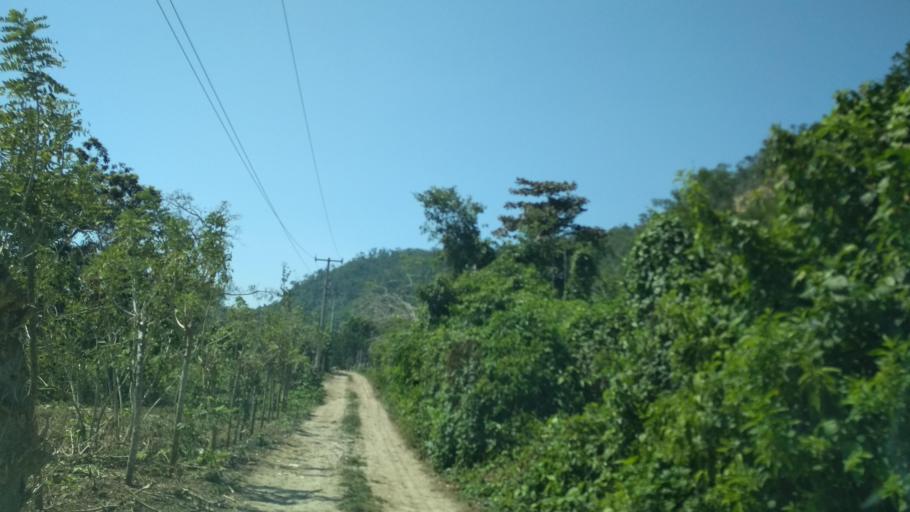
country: MX
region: Veracruz
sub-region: Papantla
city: Polutla
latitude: 20.4714
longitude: -97.2218
